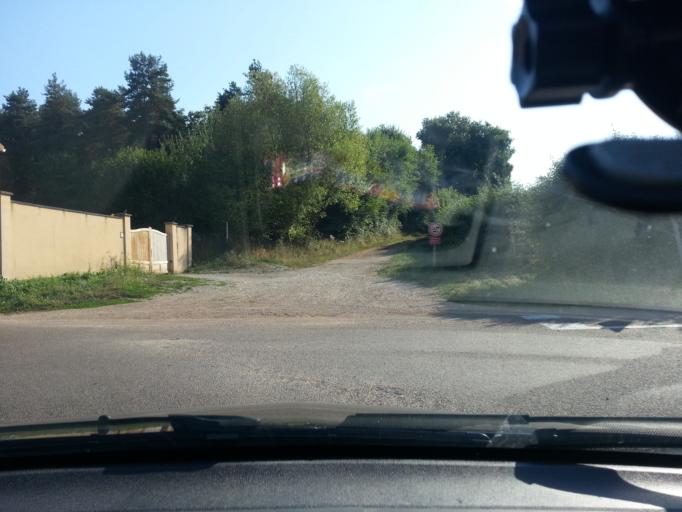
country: FR
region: Bourgogne
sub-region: Departement de Saone-et-Loire
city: Saint-Remy
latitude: 46.7596
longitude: 4.8118
